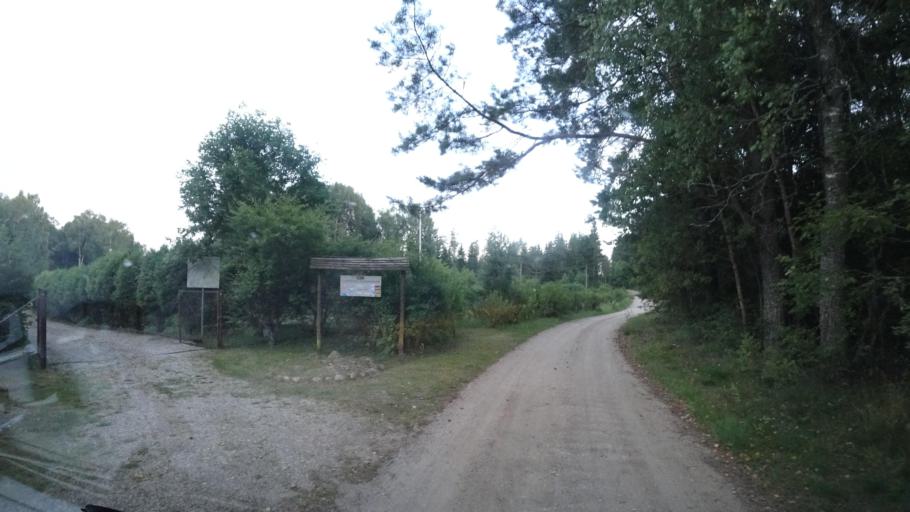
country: LT
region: Vilnius County
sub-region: Trakai
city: Rudiskes
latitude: 54.5077
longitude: 24.8895
